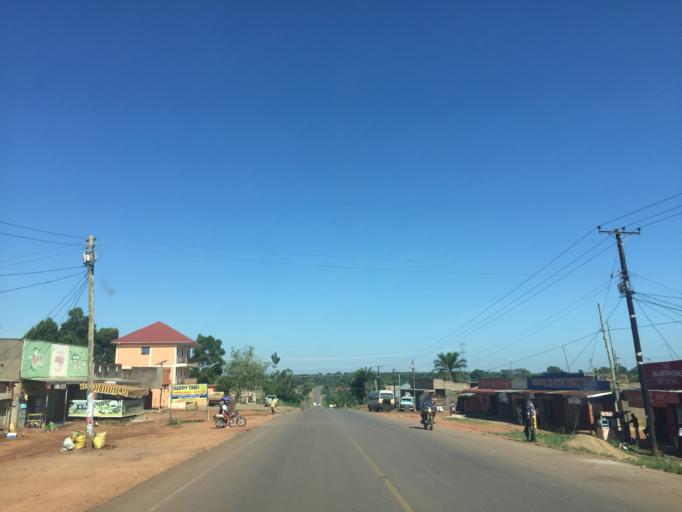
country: UG
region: Central Region
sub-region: Luwero District
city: Wobulenzi
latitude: 0.7340
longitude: 32.5245
